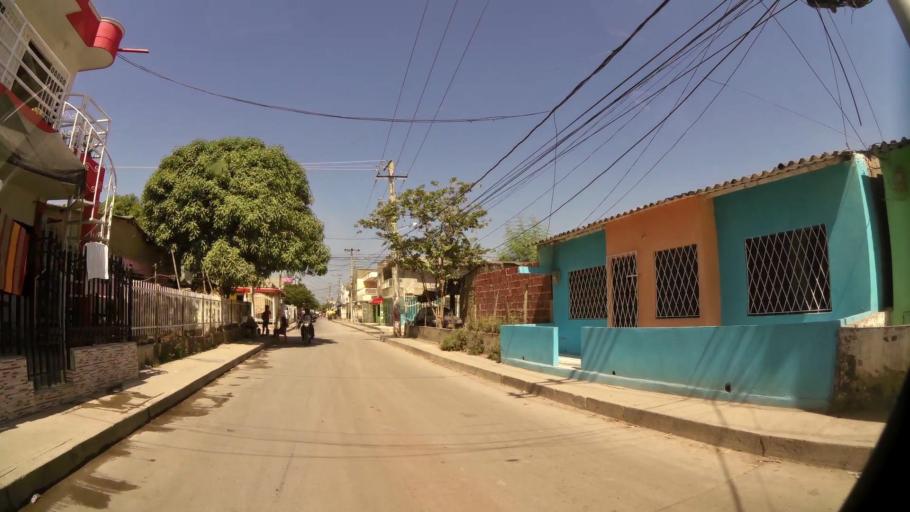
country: CO
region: Bolivar
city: Cartagena
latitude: 10.3840
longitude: -75.4558
